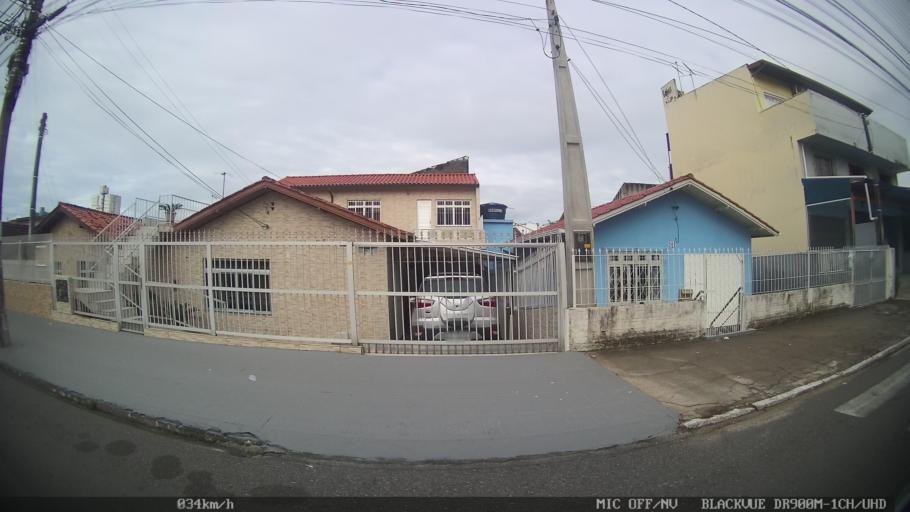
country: BR
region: Santa Catarina
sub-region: Sao Jose
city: Campinas
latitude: -27.5692
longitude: -48.6153
